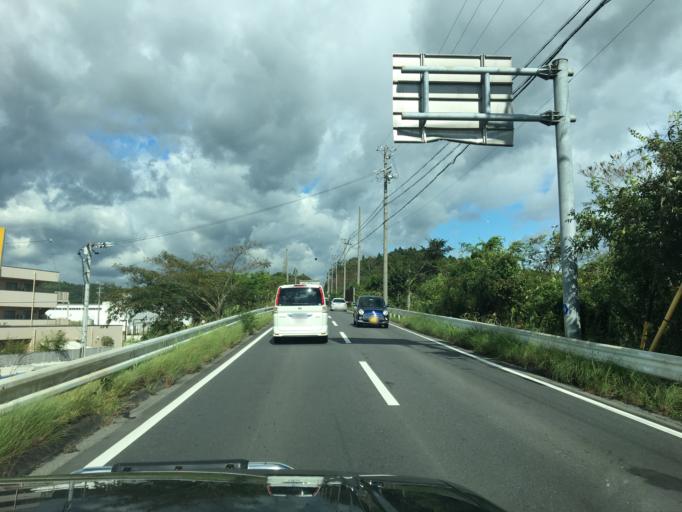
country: JP
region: Mie
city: Ueno-ebisumachi
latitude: 34.8115
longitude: 136.1847
